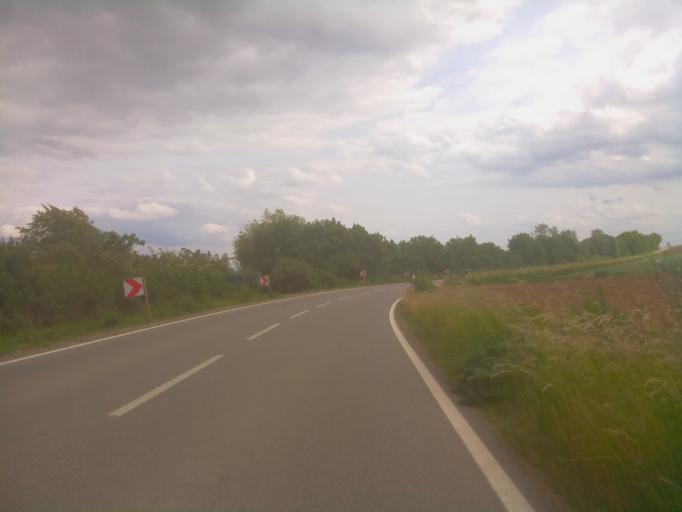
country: DE
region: Rheinland-Pfalz
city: Gerolsheim
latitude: 49.5367
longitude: 8.2792
